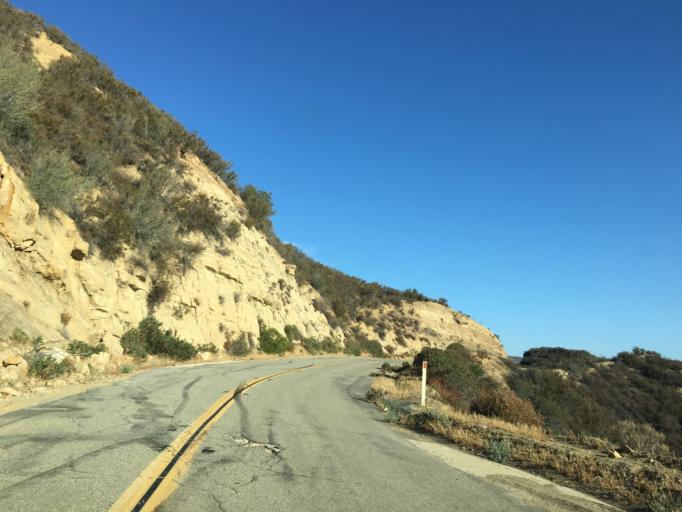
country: US
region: California
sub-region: Los Angeles County
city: Castaic
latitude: 34.5744
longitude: -118.6684
